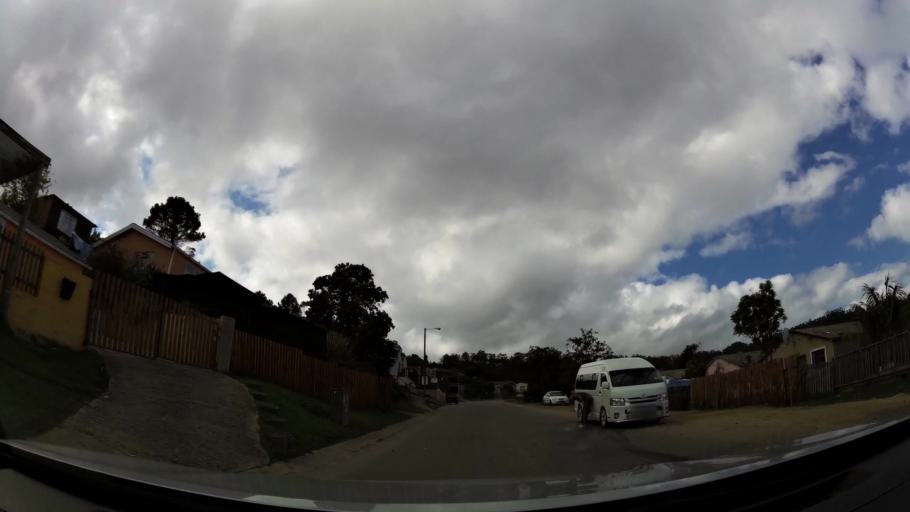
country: ZA
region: Western Cape
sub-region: Eden District Municipality
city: Knysna
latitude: -34.0515
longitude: 23.1002
